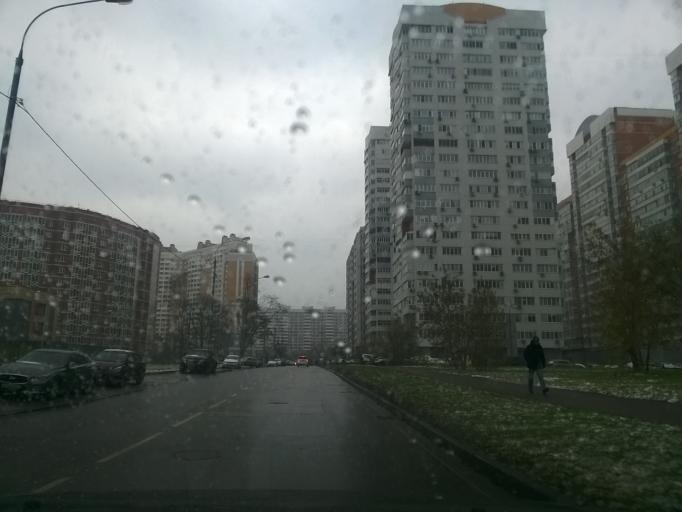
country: RU
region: Moskovskaya
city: Bol'shaya Setun'
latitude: 55.7355
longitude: 37.4303
